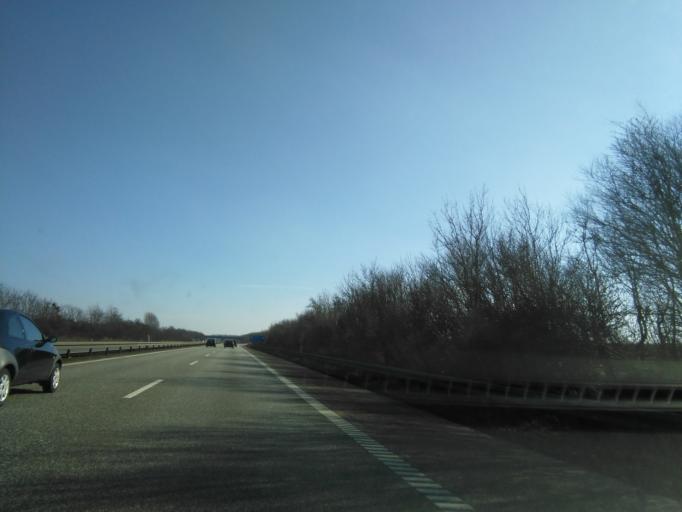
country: DK
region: South Denmark
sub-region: Kerteminde Kommune
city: Langeskov
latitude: 55.3578
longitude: 10.5547
